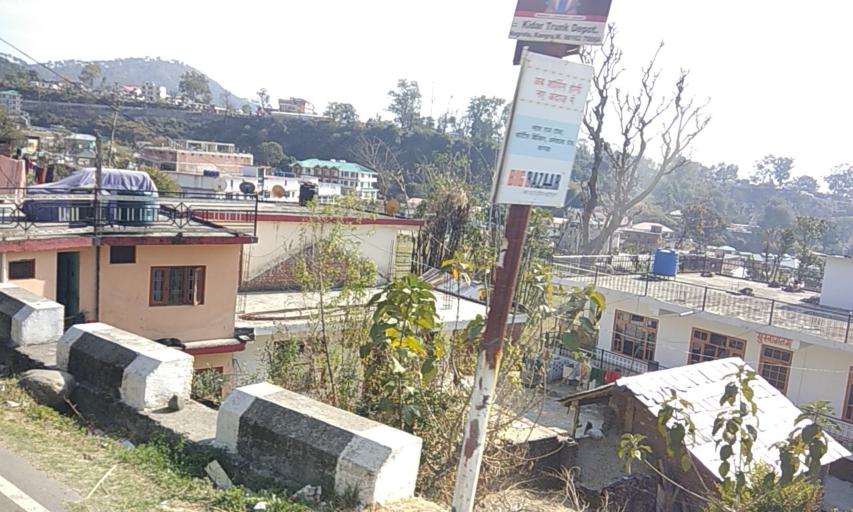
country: IN
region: Himachal Pradesh
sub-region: Kangra
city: Dharmsala
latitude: 32.1507
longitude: 76.4187
